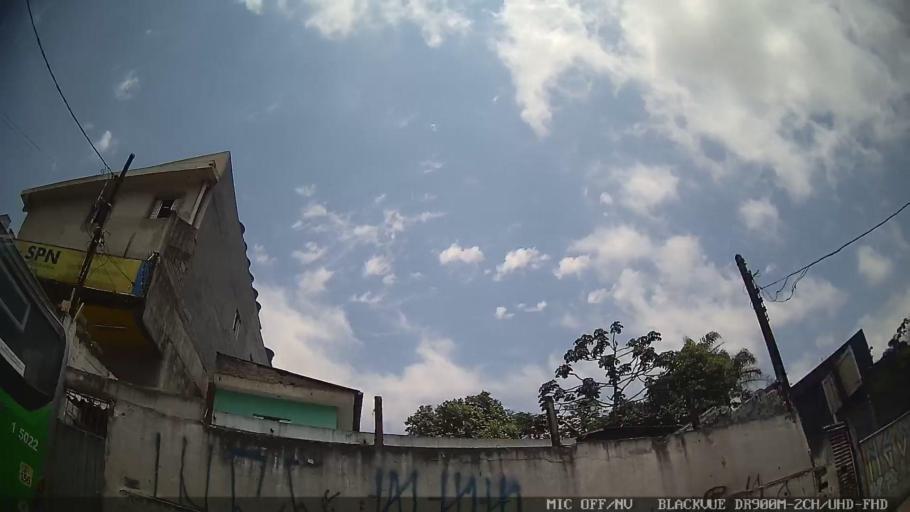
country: BR
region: Sao Paulo
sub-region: Caieiras
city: Caieiras
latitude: -23.4306
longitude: -46.7207
